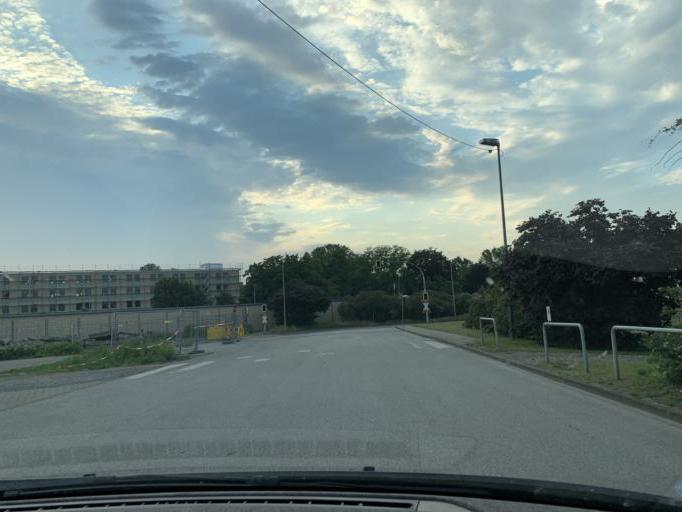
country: DE
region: North Rhine-Westphalia
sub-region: Regierungsbezirk Dusseldorf
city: Dusseldorf
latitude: 51.2219
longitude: 6.7353
